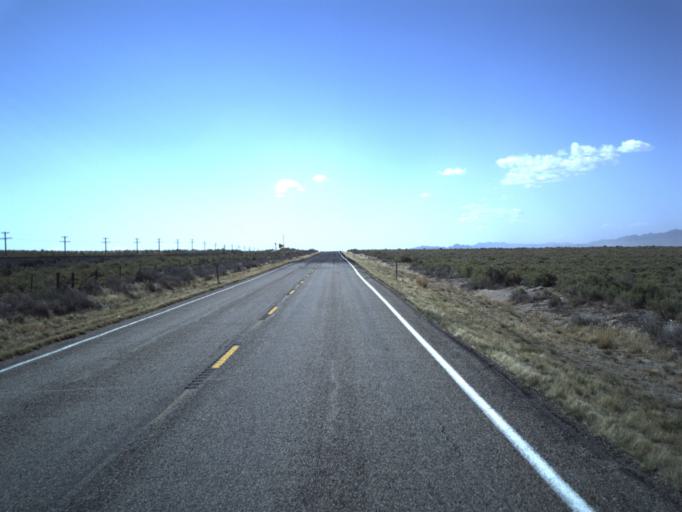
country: US
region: Utah
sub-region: Beaver County
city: Milford
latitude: 38.6888
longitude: -112.9759
